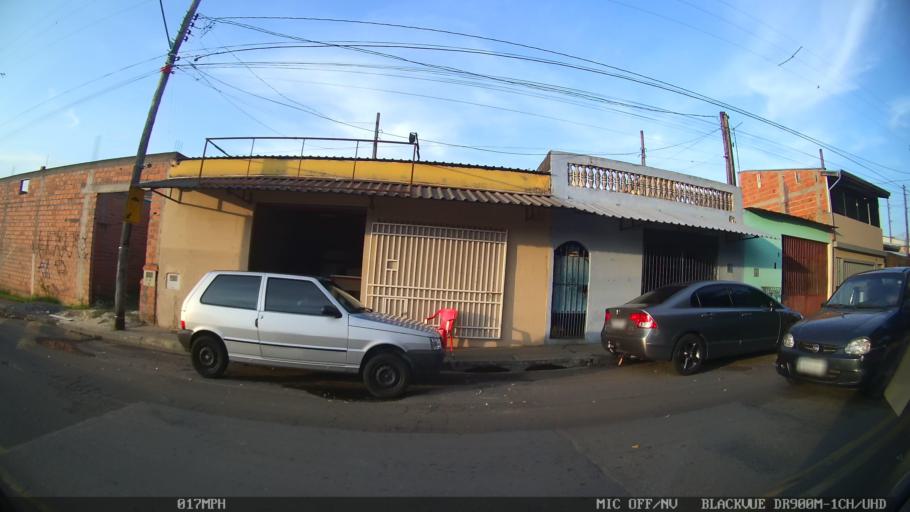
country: BR
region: Sao Paulo
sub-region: Campinas
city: Campinas
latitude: -22.9798
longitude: -47.1400
